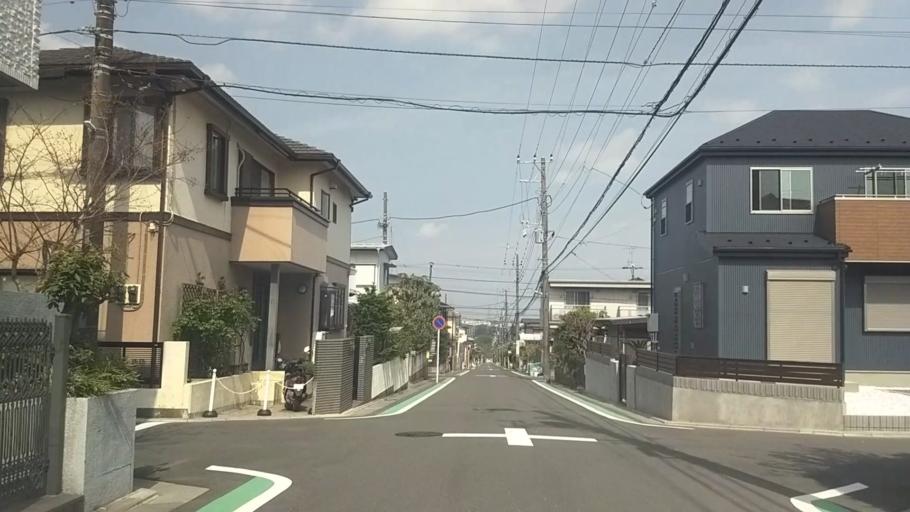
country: JP
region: Kanagawa
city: Yokohama
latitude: 35.3710
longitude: 139.6167
